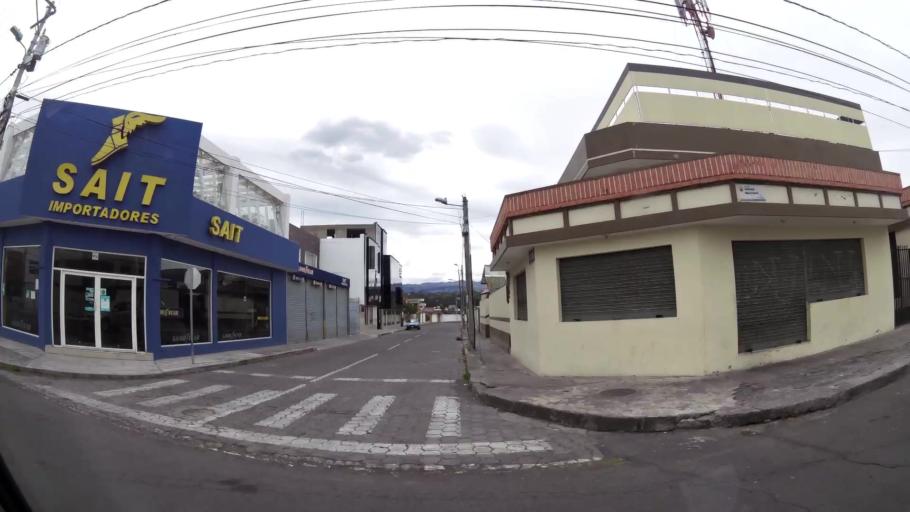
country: EC
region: Cotopaxi
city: Latacunga
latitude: -0.9437
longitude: -78.6115
